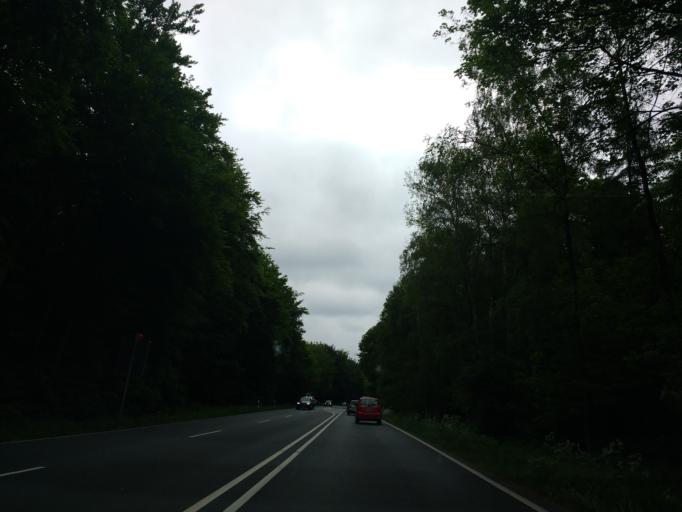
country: DE
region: Lower Saxony
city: Gross Munzel
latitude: 52.4129
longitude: 9.5033
